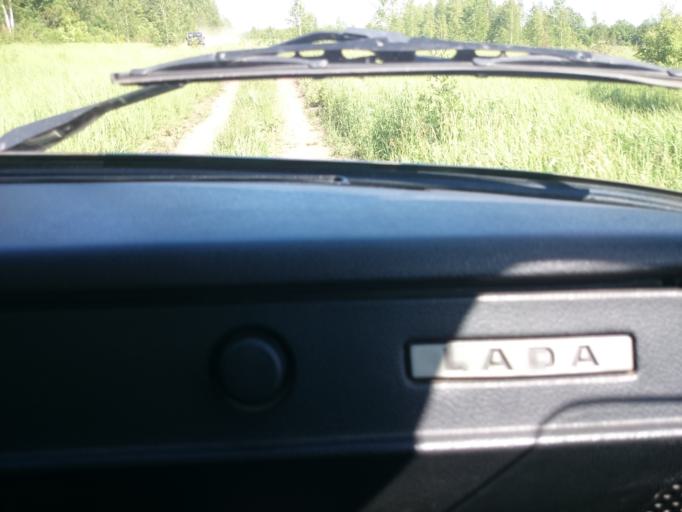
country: RU
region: Mordoviya
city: Kadoshkino
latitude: 54.0523
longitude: 44.4843
